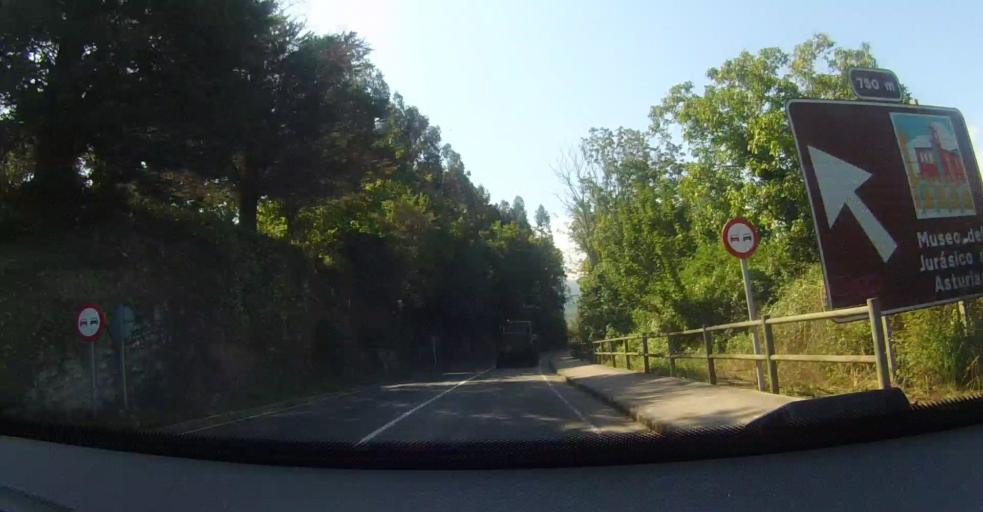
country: ES
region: Asturias
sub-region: Province of Asturias
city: Colunga
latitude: 43.4881
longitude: -5.2764
